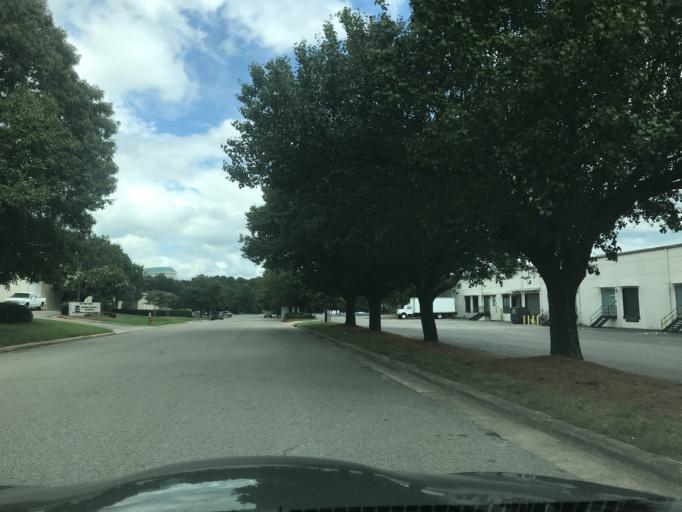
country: US
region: North Carolina
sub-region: Wake County
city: Raleigh
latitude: 35.8218
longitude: -78.6166
